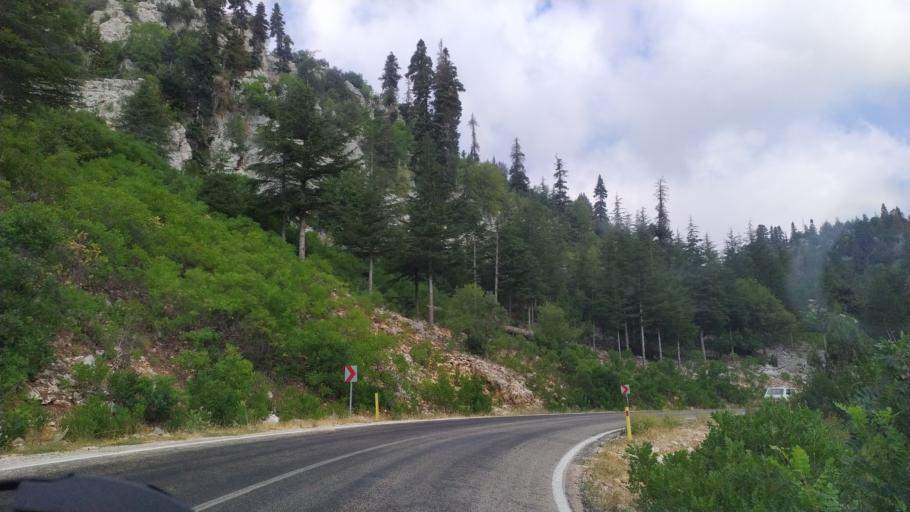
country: TR
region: Mersin
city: Kirobasi
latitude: 36.6045
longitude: 33.8862
